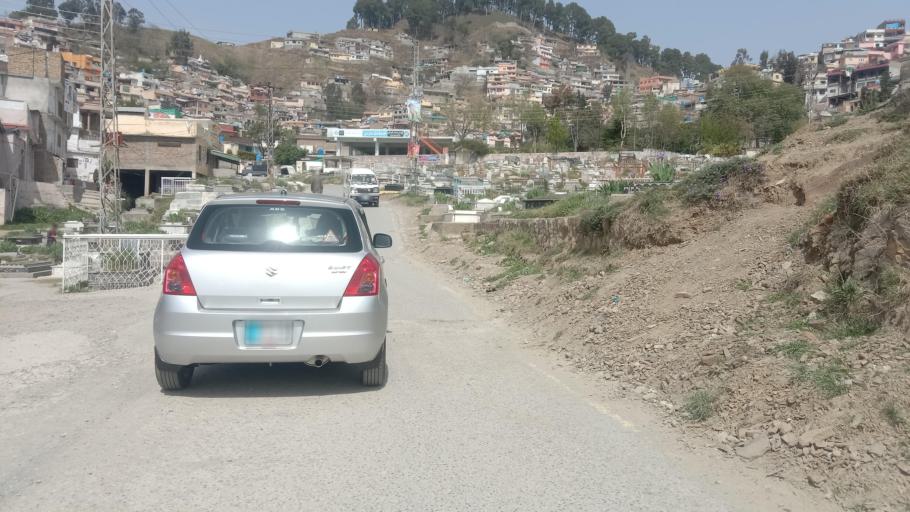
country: PK
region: Khyber Pakhtunkhwa
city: Abbottabad
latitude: 34.1492
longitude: 73.2019
